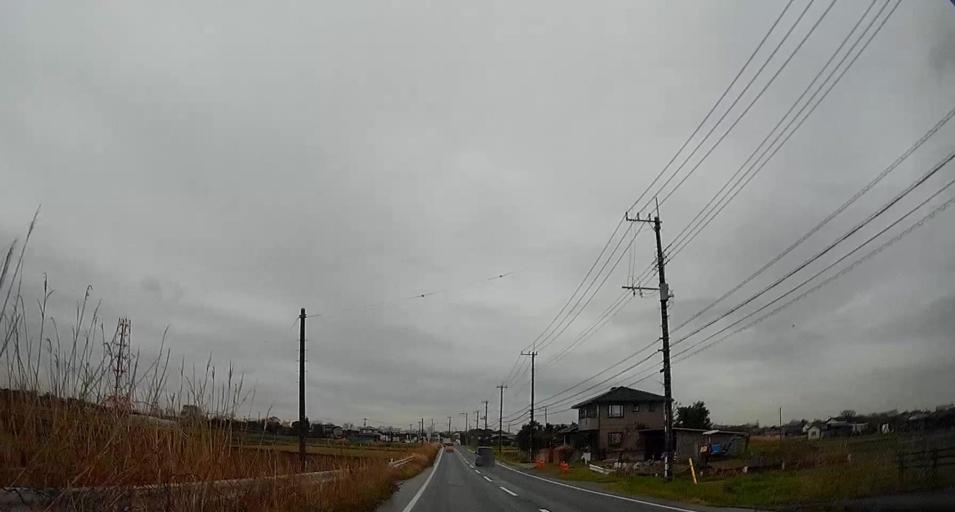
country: JP
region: Chiba
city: Kisarazu
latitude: 35.4292
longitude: 139.9446
